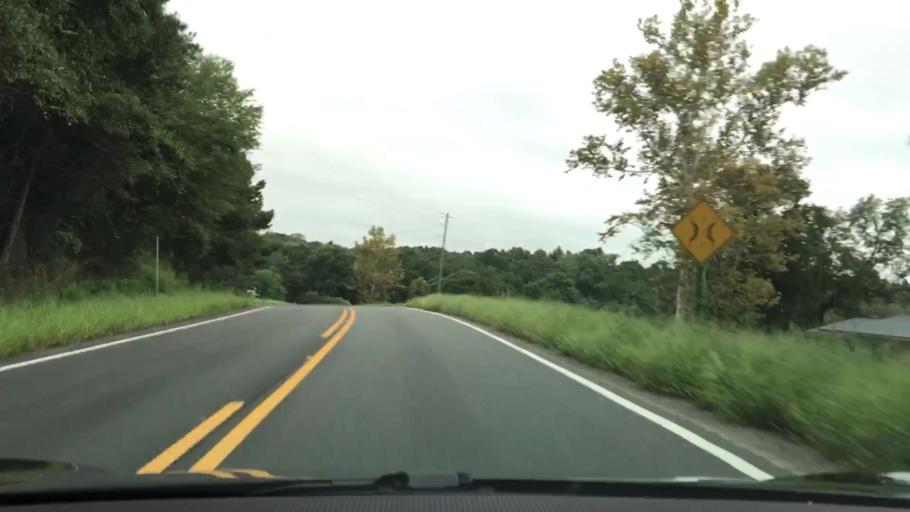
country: US
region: Alabama
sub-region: Covington County
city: Opp
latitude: 31.2227
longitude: -86.1602
